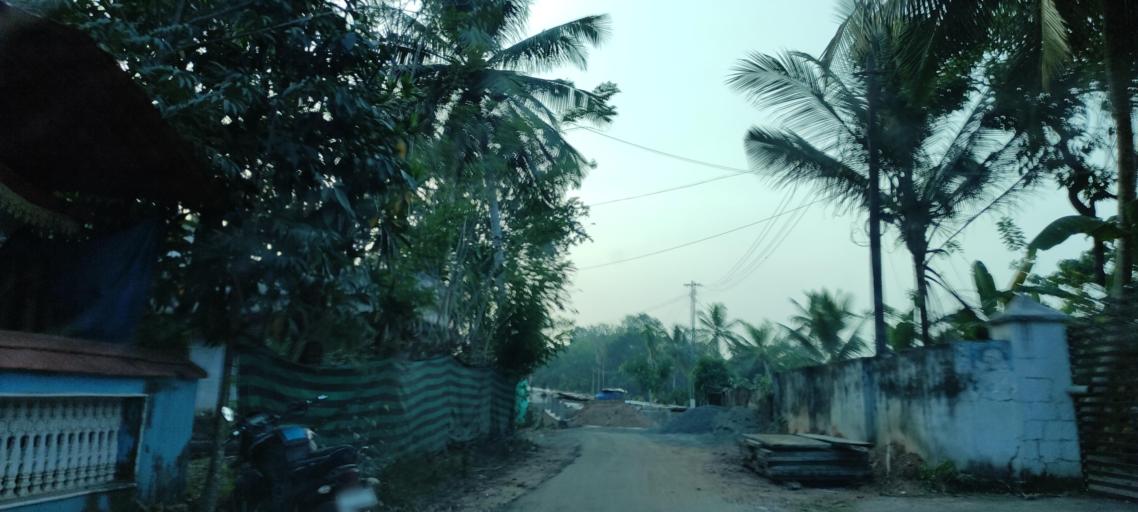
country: IN
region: Kerala
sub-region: Alappuzha
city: Mavelikara
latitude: 9.2767
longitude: 76.5499
